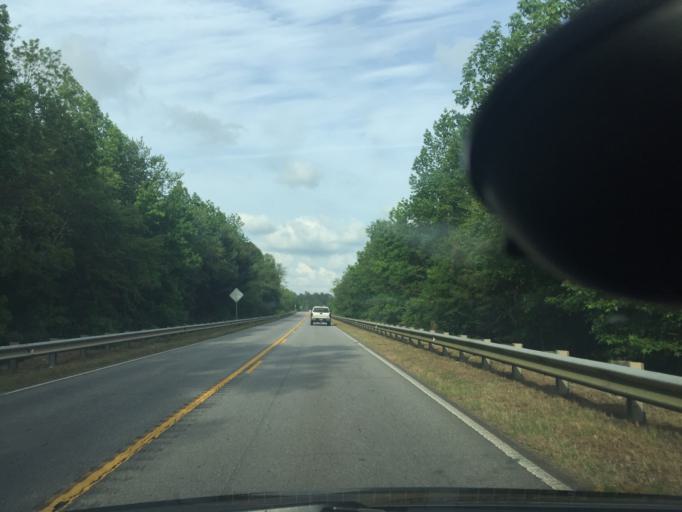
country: US
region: Georgia
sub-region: Chatham County
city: Bloomingdale
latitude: 32.0798
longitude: -81.3828
